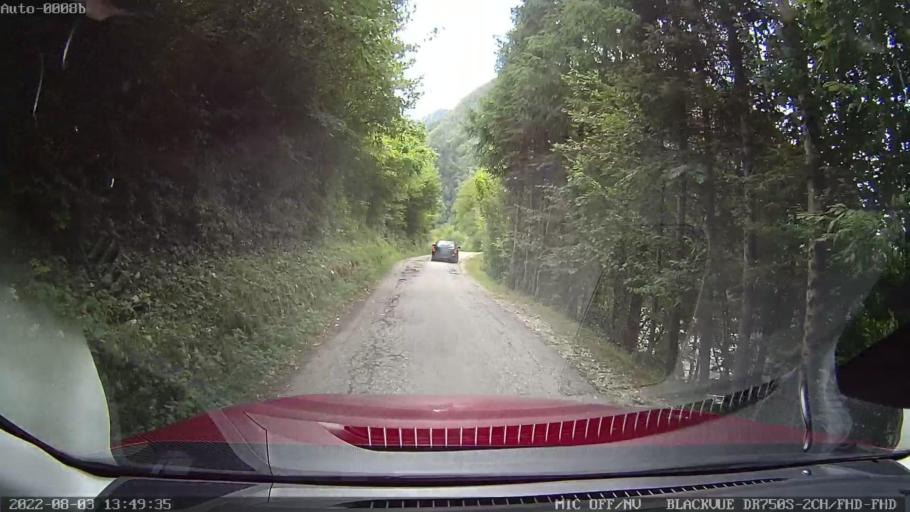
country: SI
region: Bovec
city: Bovec
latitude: 46.3410
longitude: 13.6850
